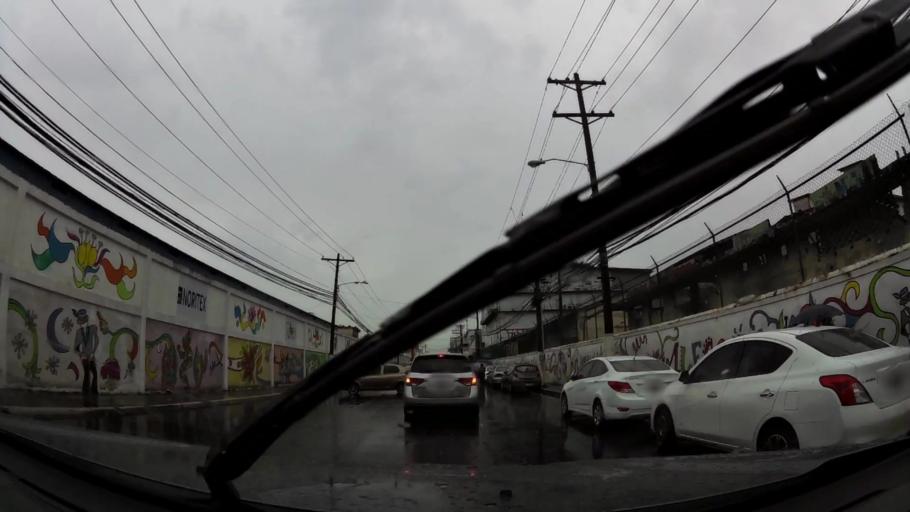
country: PA
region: Colon
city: Colon
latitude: 9.3547
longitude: -79.8977
